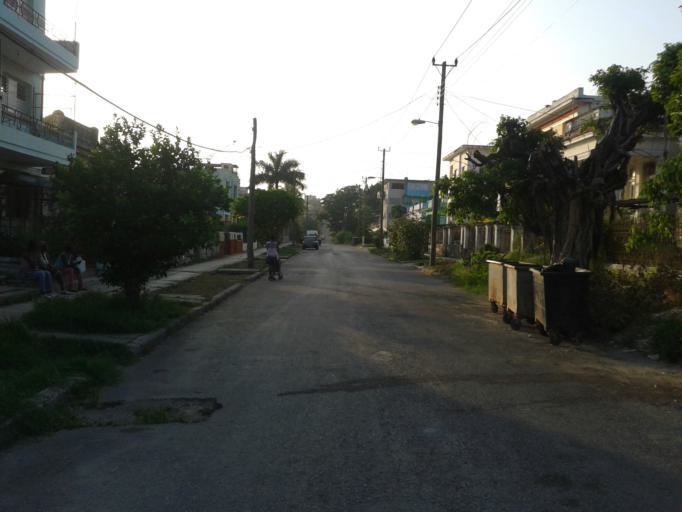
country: CU
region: La Habana
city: Cerro
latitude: 23.0925
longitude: -82.3756
